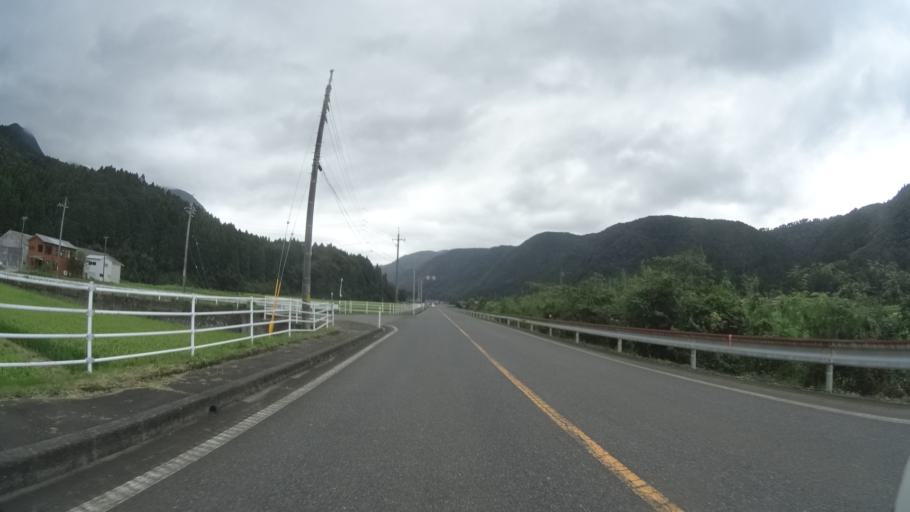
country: JP
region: Tottori
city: Tottori
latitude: 35.4522
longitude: 134.0368
